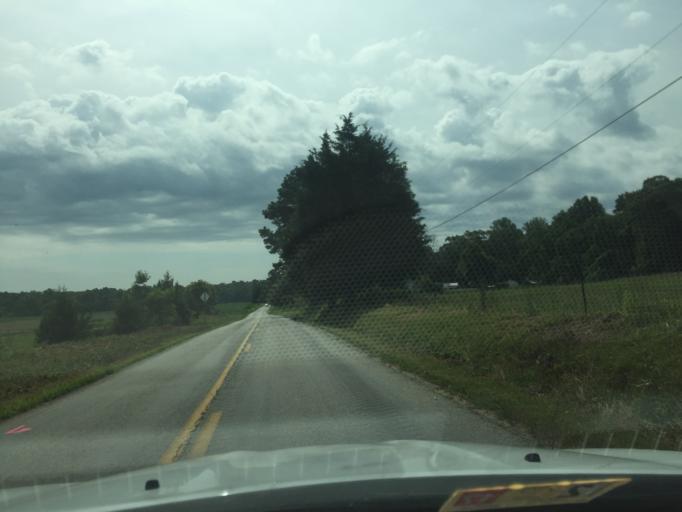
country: US
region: Virginia
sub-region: Charles City County
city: Charles City
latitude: 37.4131
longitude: -77.0435
